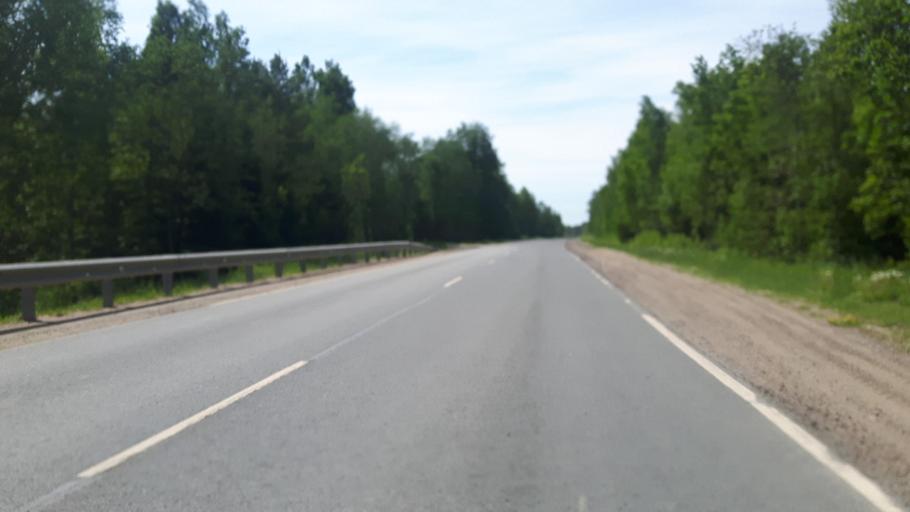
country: RU
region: Leningrad
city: Vistino
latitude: 59.6803
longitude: 28.4560
